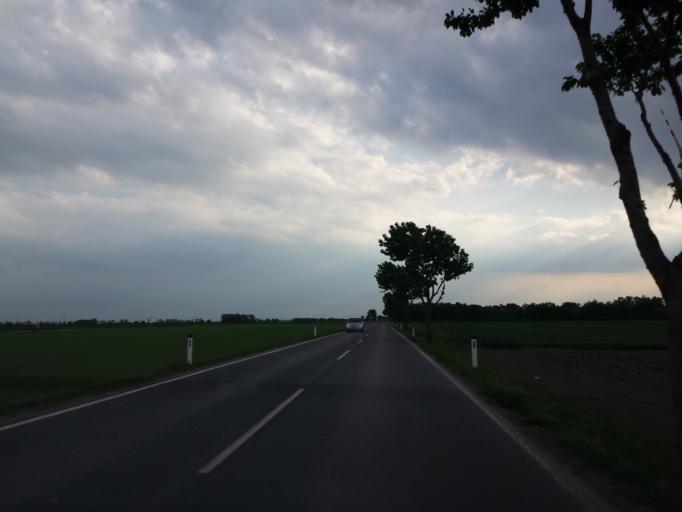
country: AT
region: Lower Austria
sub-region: Politischer Bezirk Ganserndorf
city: Grosshofen
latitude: 48.2514
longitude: 16.6084
